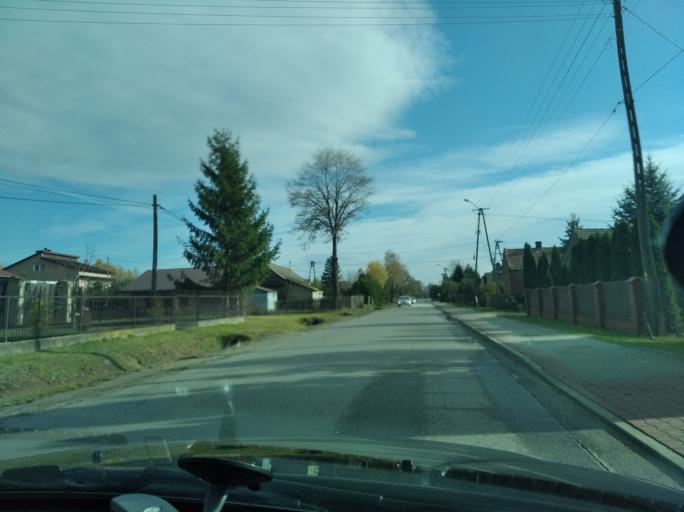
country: PL
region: Subcarpathian Voivodeship
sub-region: Powiat ropczycko-sedziszowski
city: Ostrow
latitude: 50.1007
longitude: 21.6068
